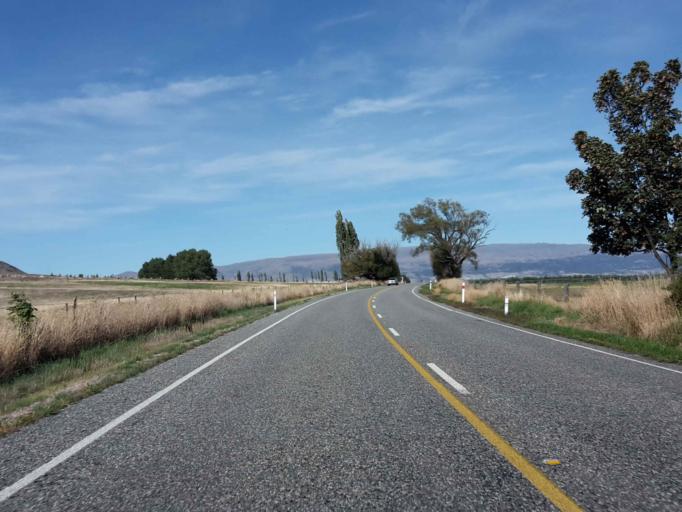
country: NZ
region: Otago
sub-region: Queenstown-Lakes District
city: Wanaka
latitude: -44.7735
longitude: 169.3510
